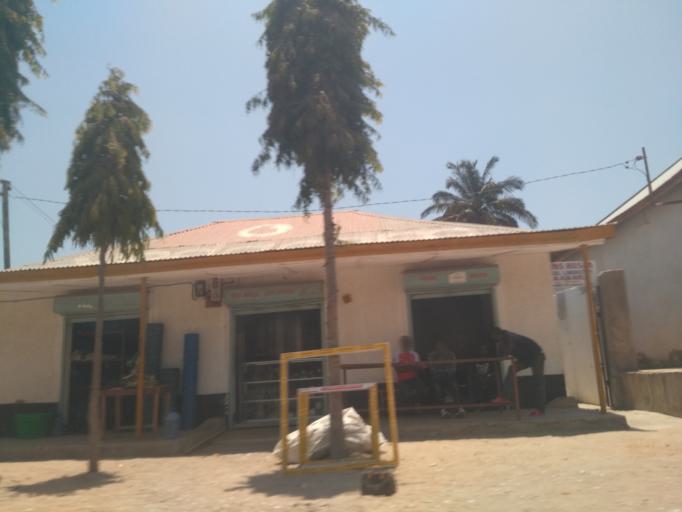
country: TZ
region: Dodoma
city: Dodoma
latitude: -6.1760
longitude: 35.7462
